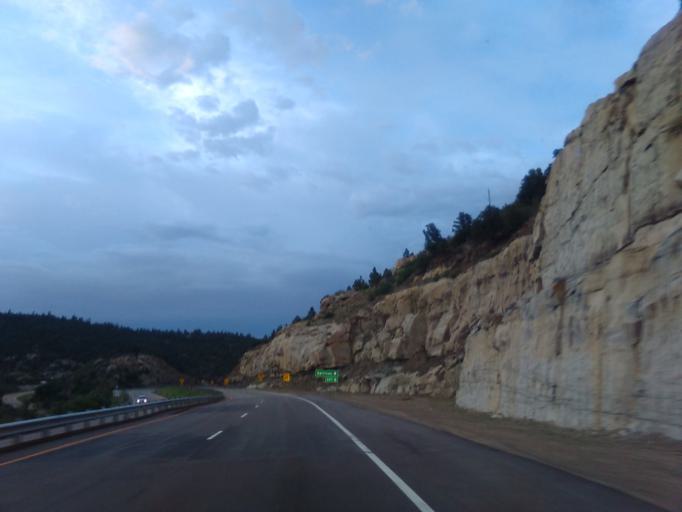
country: US
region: Colorado
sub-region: Las Animas County
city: Trinidad
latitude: 37.0568
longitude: -104.5227
